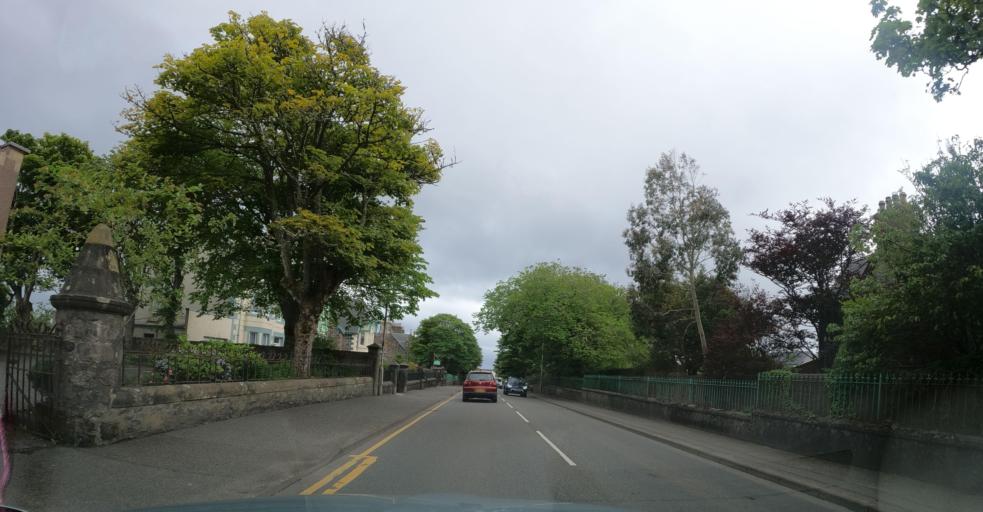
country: GB
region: Scotland
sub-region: Eilean Siar
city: Stornoway
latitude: 58.2108
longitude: -6.3826
